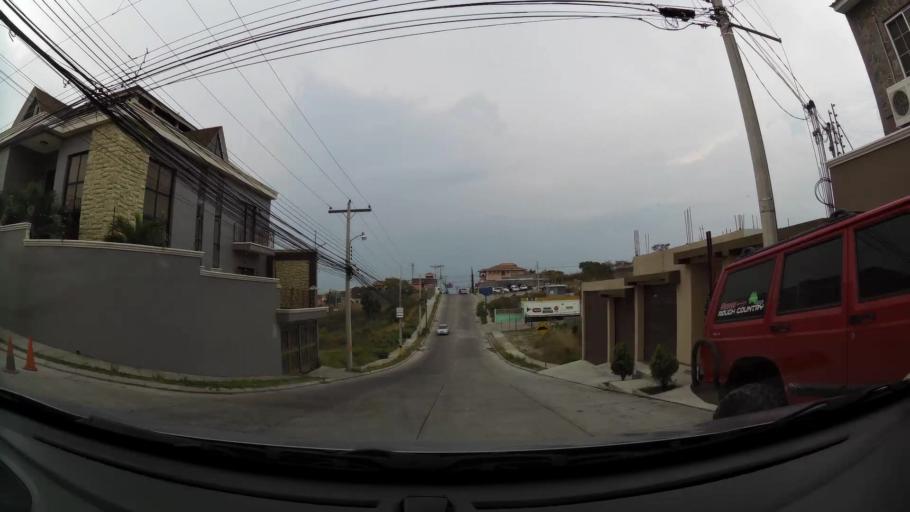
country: HN
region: Francisco Morazan
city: Yaguacire
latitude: 14.0517
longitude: -87.2424
